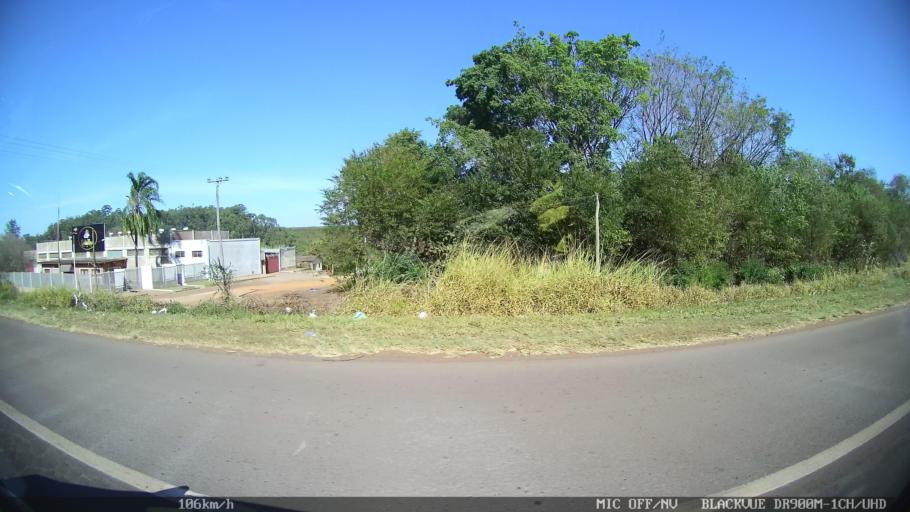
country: BR
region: Sao Paulo
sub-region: Batatais
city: Batatais
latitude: -20.9063
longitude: -47.5979
